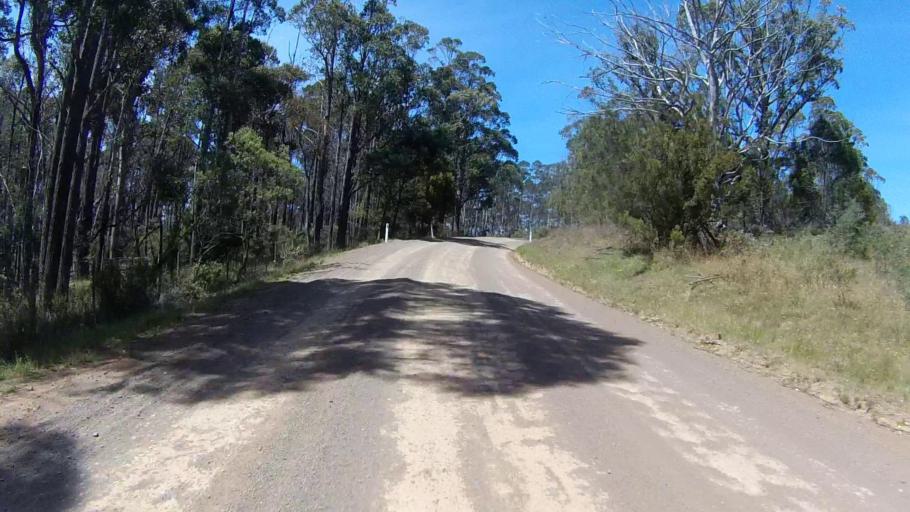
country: AU
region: Tasmania
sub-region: Sorell
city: Sorell
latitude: -42.7268
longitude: 147.7419
